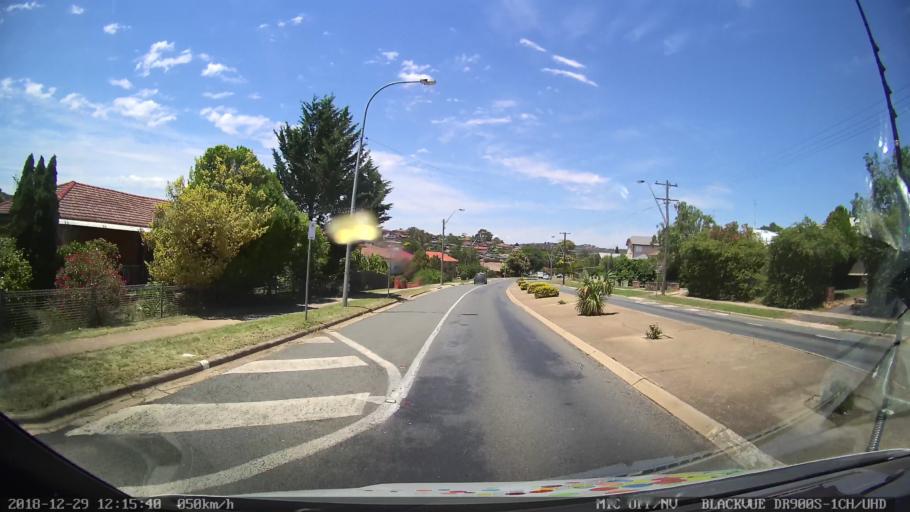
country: AU
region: New South Wales
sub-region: Queanbeyan
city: Queanbeyan
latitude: -35.3635
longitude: 149.2340
